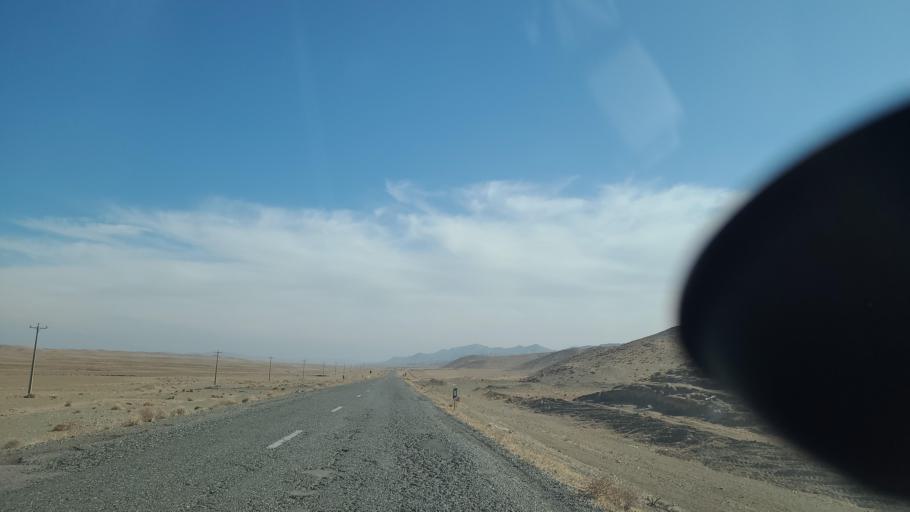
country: IR
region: Razavi Khorasan
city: Fariman
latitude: 35.5912
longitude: 59.6055
